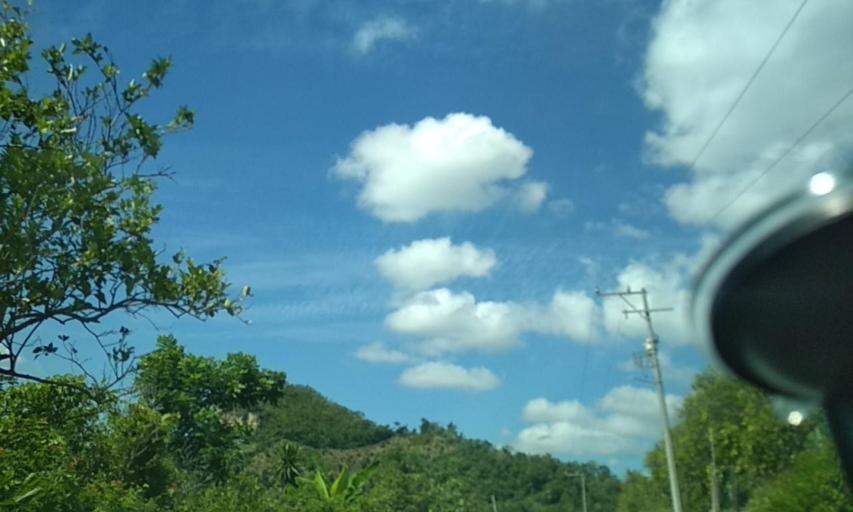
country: MX
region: Veracruz
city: Cazones de Herrera
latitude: 20.6218
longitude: -97.3238
